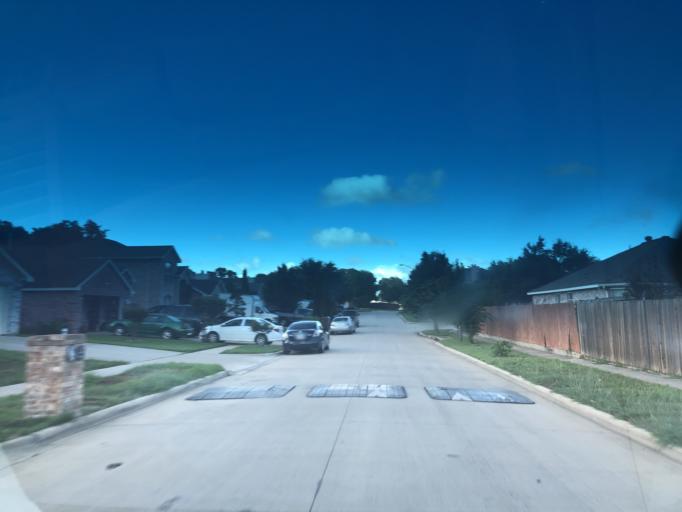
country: US
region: Texas
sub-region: Dallas County
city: Irving
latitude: 32.8086
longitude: -97.0034
